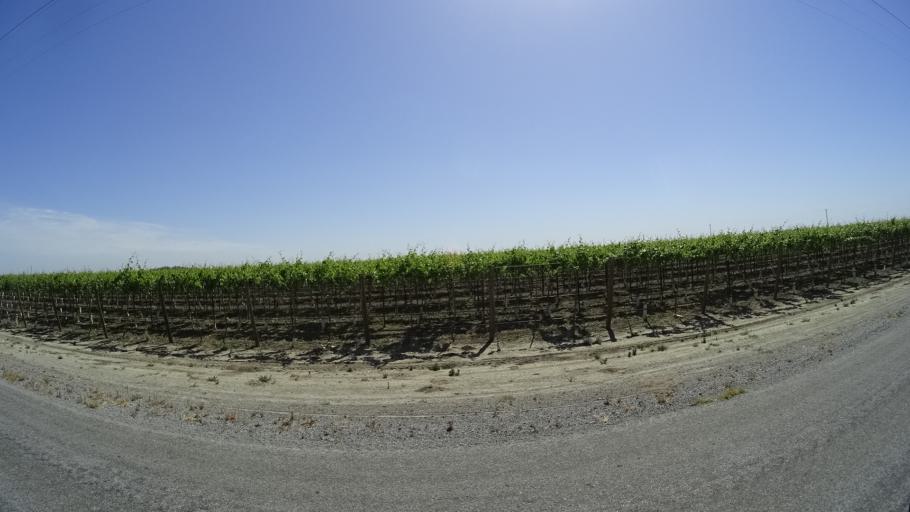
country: US
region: California
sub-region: Kings County
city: Stratford
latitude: 36.2347
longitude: -119.8343
